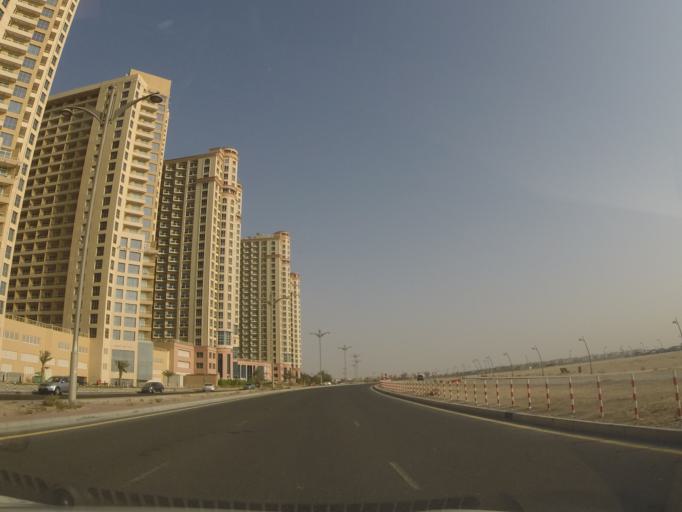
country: AE
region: Dubai
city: Dubai
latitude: 25.0349
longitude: 55.2019
